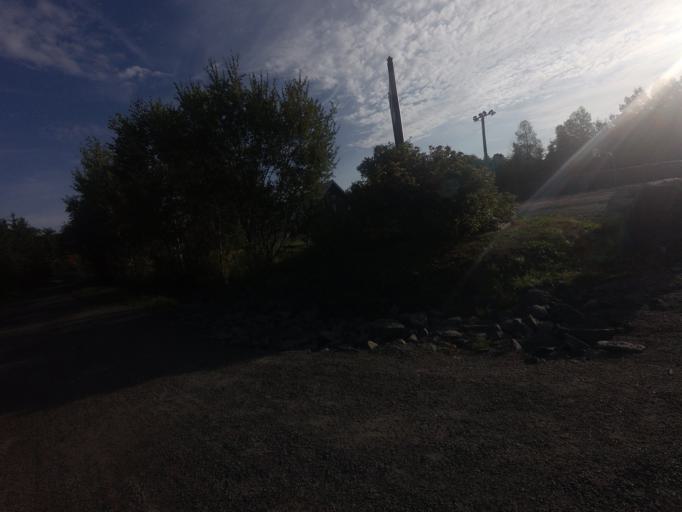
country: CA
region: Quebec
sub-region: Laurentides
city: Sainte-Adele
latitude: 45.9362
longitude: -74.1235
